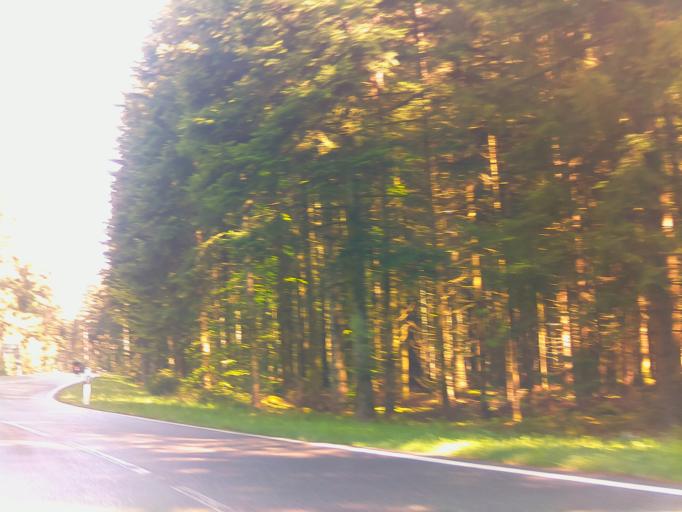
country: DE
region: Baden-Wuerttemberg
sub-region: Karlsruhe Region
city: Neuweiler
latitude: 48.6473
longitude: 8.5721
